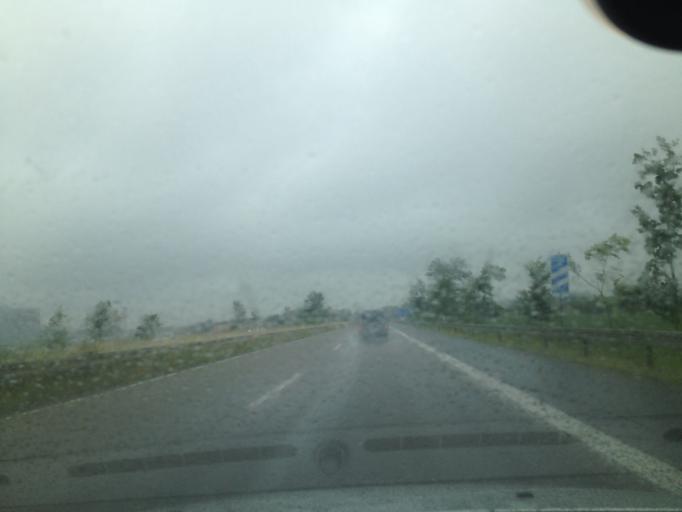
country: DE
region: Hesse
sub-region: Regierungsbezirk Darmstadt
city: Langenselbold
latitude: 50.1748
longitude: 9.0154
